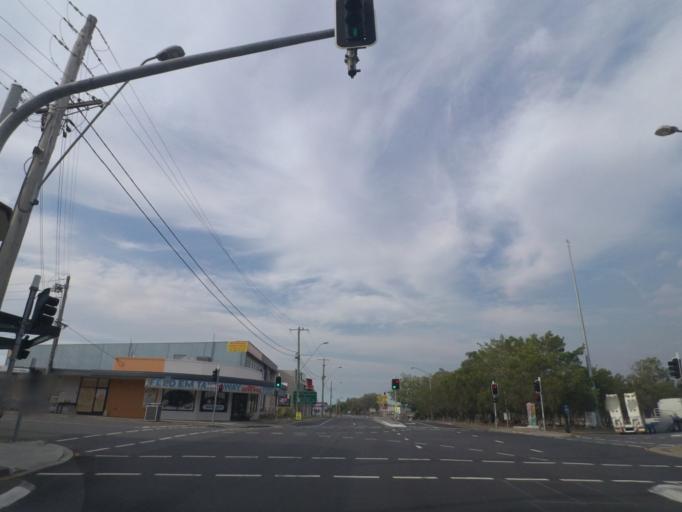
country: AU
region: Queensland
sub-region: Brisbane
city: Rocklea
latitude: -27.5430
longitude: 153.0111
